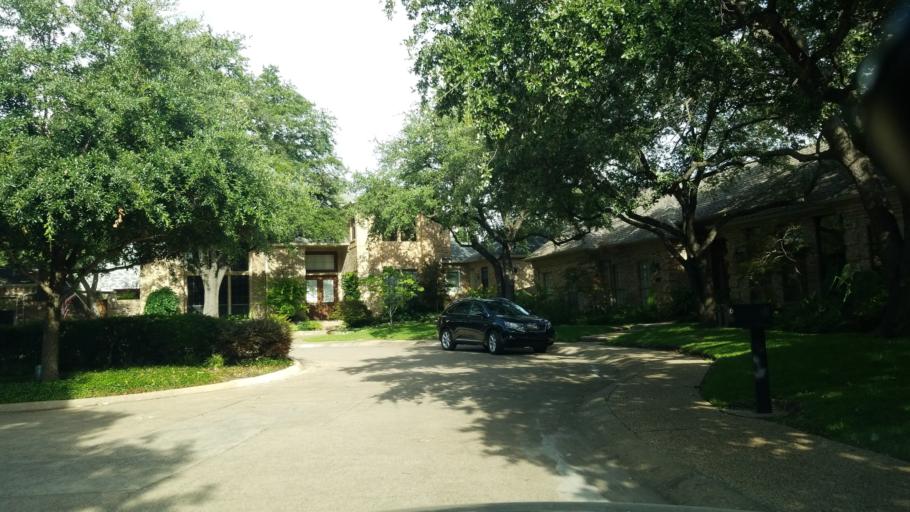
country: US
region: Texas
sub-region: Dallas County
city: University Park
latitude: 32.8703
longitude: -96.7792
